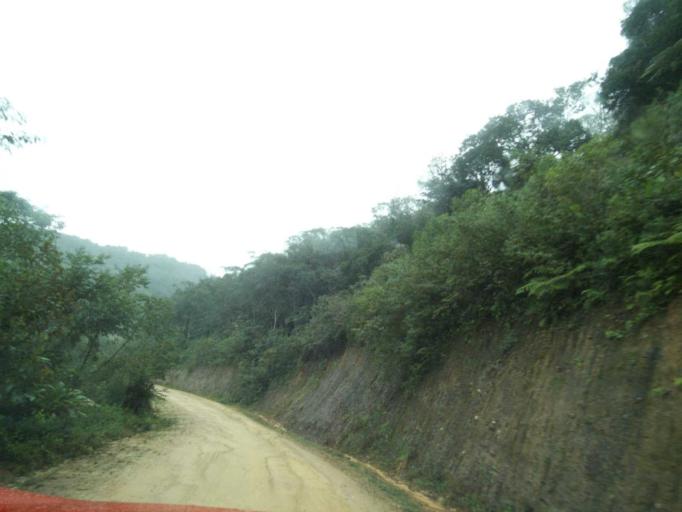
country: BR
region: Santa Catarina
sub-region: Anitapolis
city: Anitapolis
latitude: -27.9199
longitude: -49.1904
